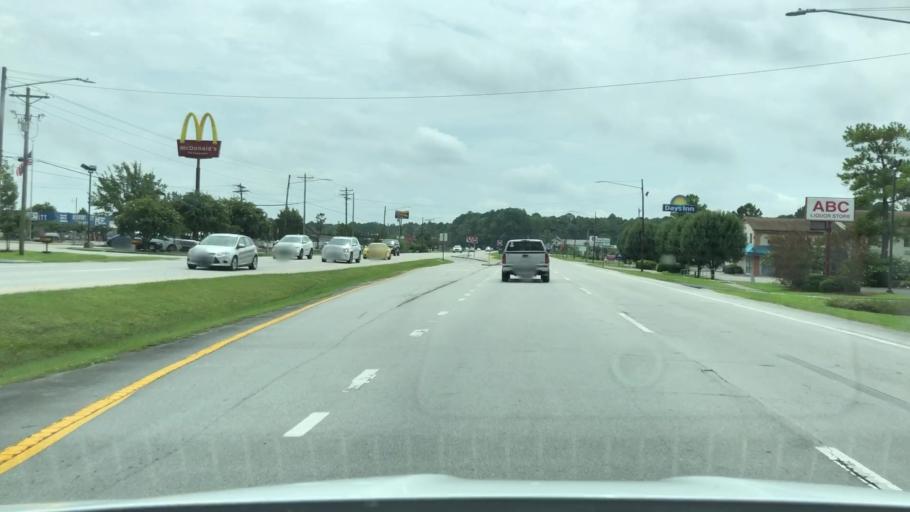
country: US
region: North Carolina
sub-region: Craven County
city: Havelock
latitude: 34.8614
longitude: -76.8977
